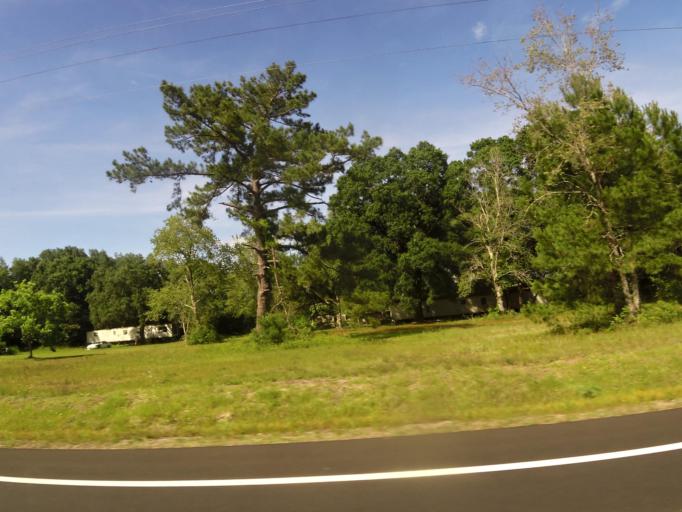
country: US
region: Florida
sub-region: Nassau County
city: Hilliard
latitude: 30.6198
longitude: -81.8848
